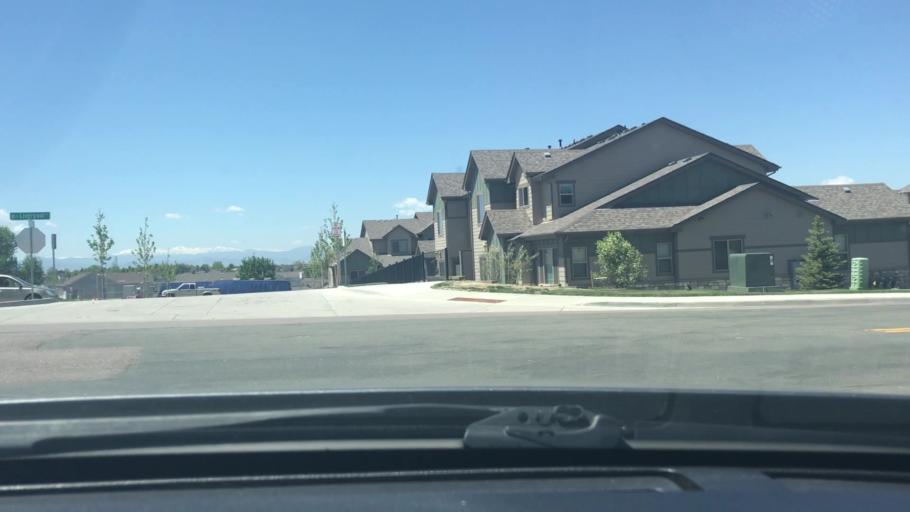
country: US
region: Colorado
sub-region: Arapahoe County
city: Dove Valley
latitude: 39.6507
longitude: -104.7437
